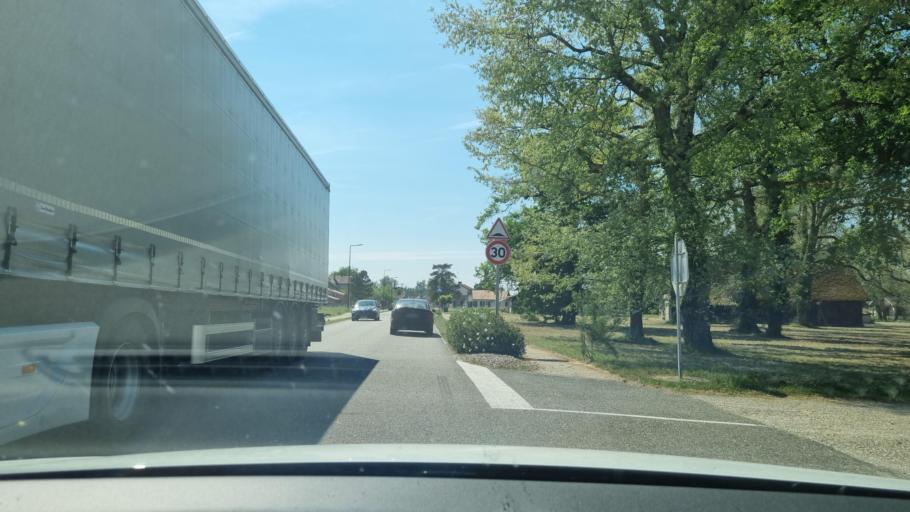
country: FR
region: Aquitaine
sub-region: Departement de la Gironde
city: Bazas
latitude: 44.2922
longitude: -0.2539
